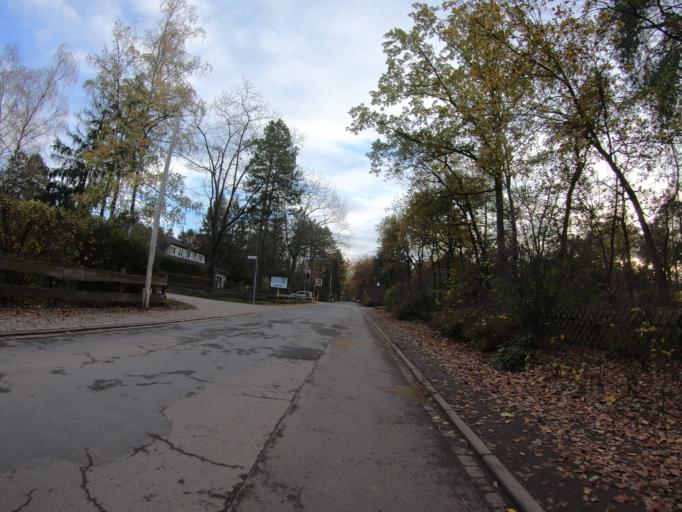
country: DE
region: Lower Saxony
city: Ribbesbuttel
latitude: 52.4593
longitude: 10.4961
